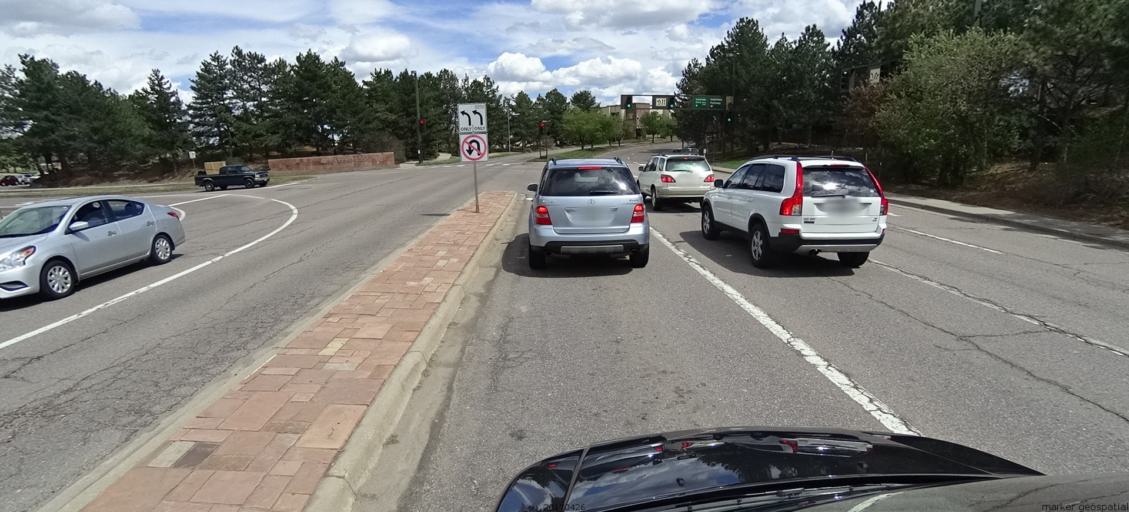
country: US
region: Colorado
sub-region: Arapahoe County
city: Centennial
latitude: 39.5661
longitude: -104.8676
